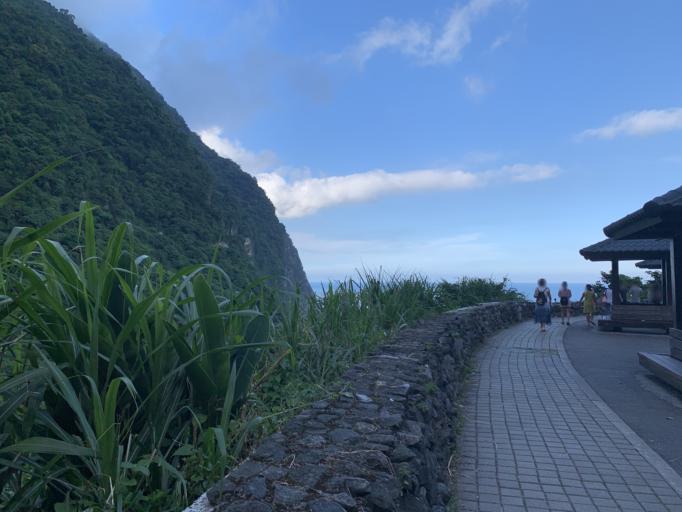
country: TW
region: Taiwan
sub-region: Hualien
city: Hualian
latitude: 24.2055
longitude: 121.6698
